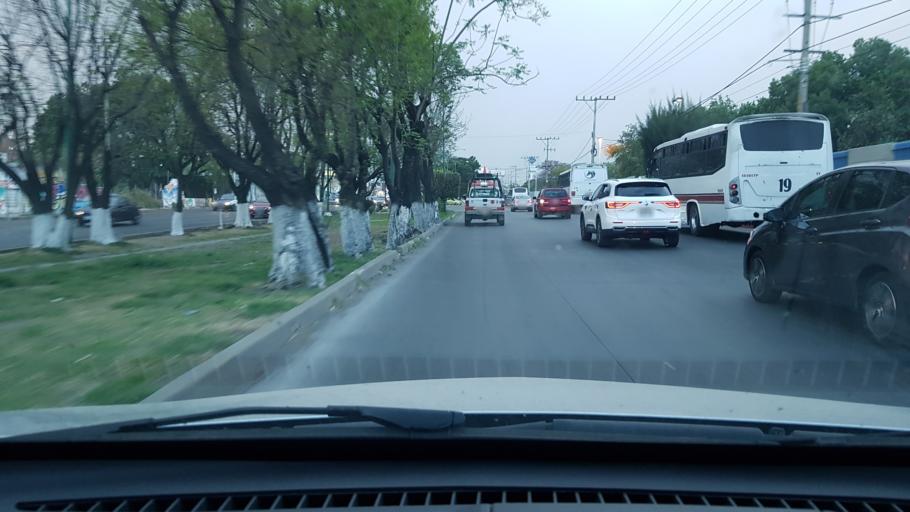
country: MX
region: Morelos
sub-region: Tepoztlan
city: Tetecolala
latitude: 18.9053
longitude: -99.1770
